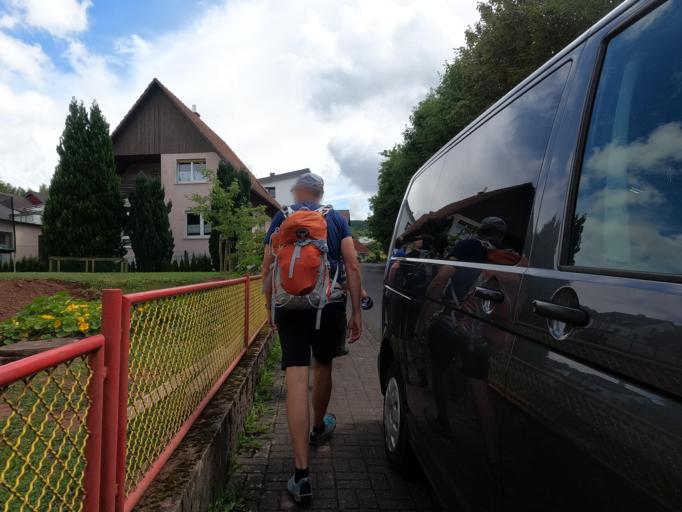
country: DE
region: Bavaria
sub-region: Regierungsbezirk Unterfranken
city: Zeitlofs
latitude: 50.3087
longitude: 9.6287
